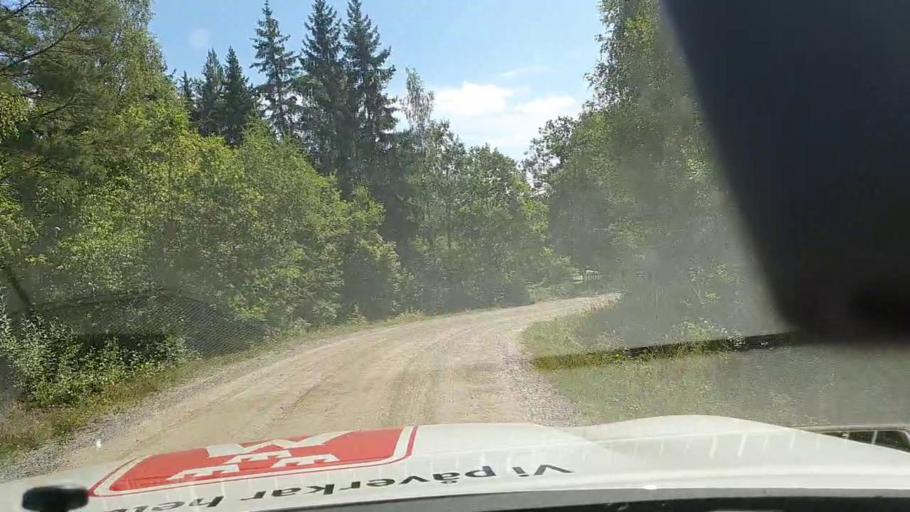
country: SE
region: Soedermanland
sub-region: Strangnas Kommun
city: Akers Styckebruk
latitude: 59.2154
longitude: 16.9101
